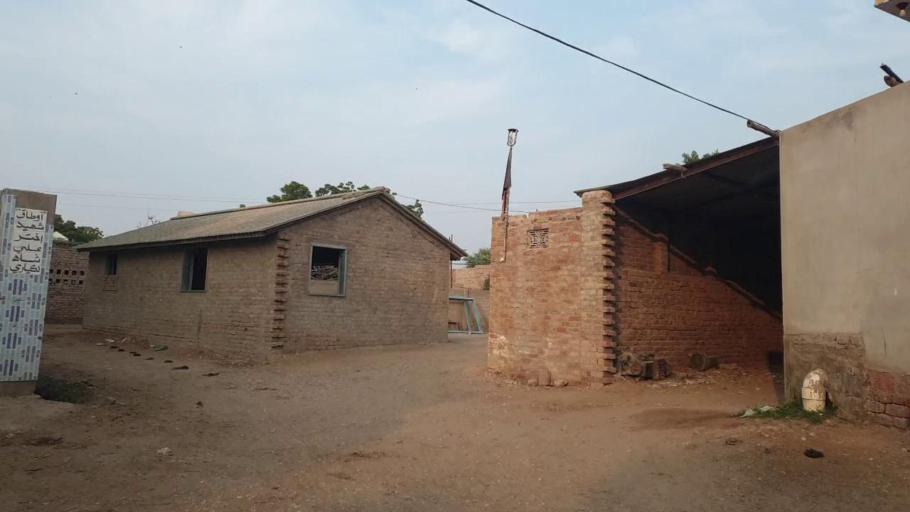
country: PK
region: Sindh
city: Sann
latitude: 26.1714
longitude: 68.0199
